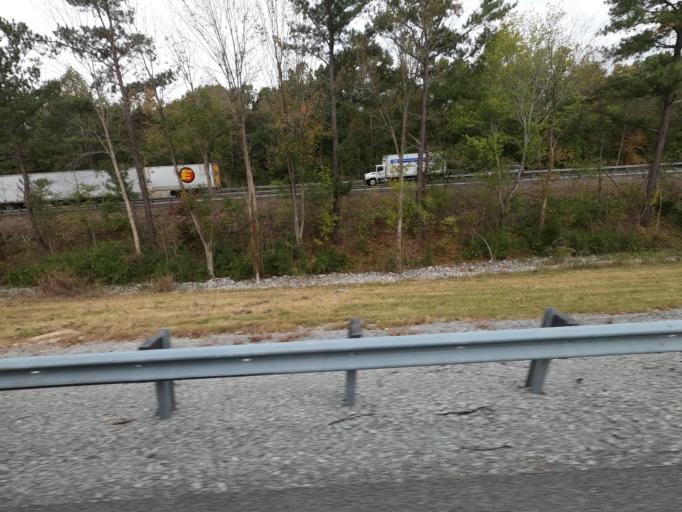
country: US
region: Tennessee
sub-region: Williamson County
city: Fairview
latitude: 36.0324
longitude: -87.1675
